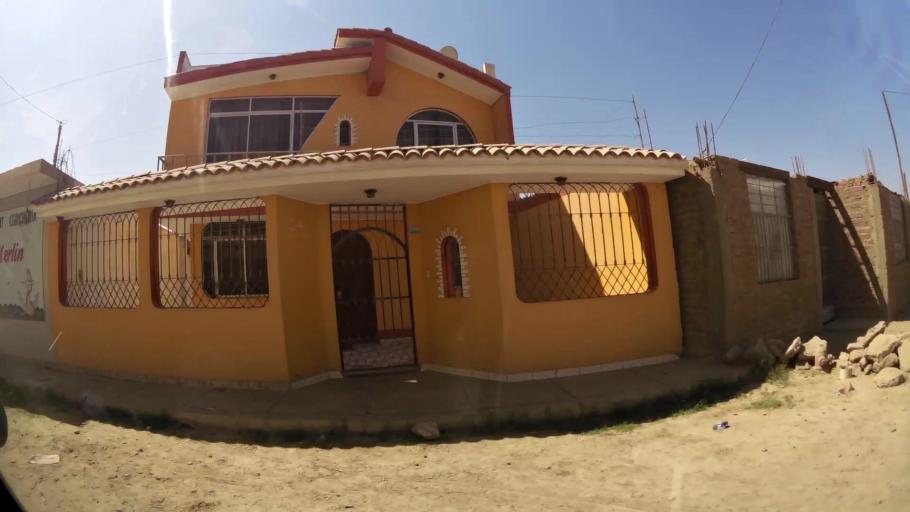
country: PE
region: Ica
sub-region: Provincia de Ica
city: Subtanjalla
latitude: -14.0383
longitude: -75.7535
